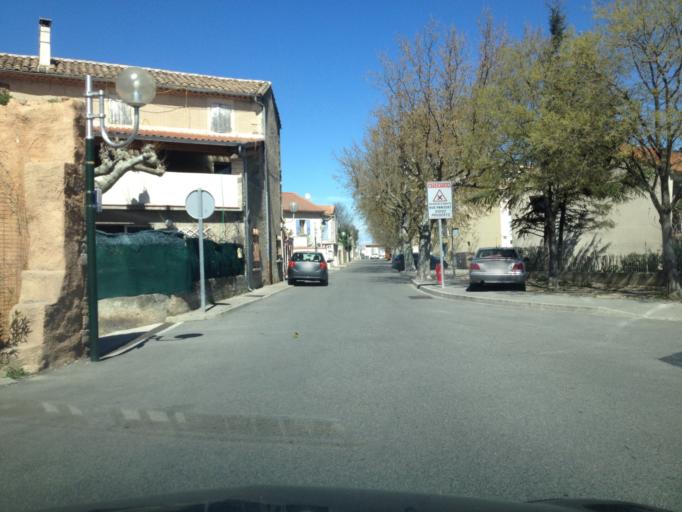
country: FR
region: Provence-Alpes-Cote d'Azur
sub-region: Departement du Vaucluse
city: Le Pontet
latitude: 43.9644
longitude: 4.8598
